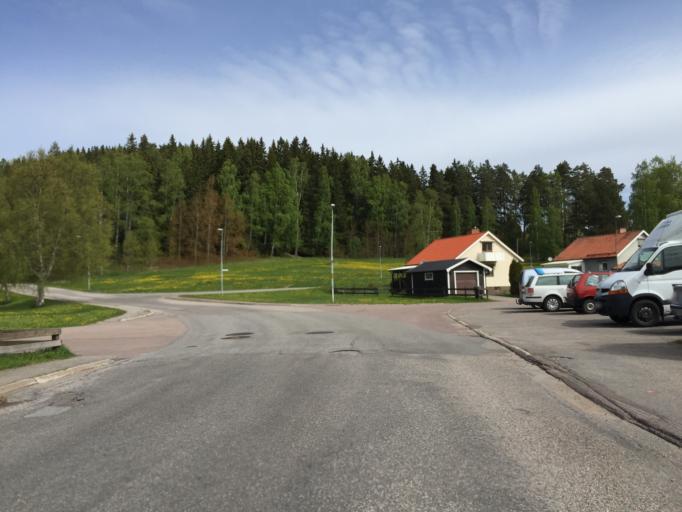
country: SE
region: Dalarna
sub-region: Ludvika Kommun
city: Ludvika
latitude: 60.1297
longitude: 15.1891
